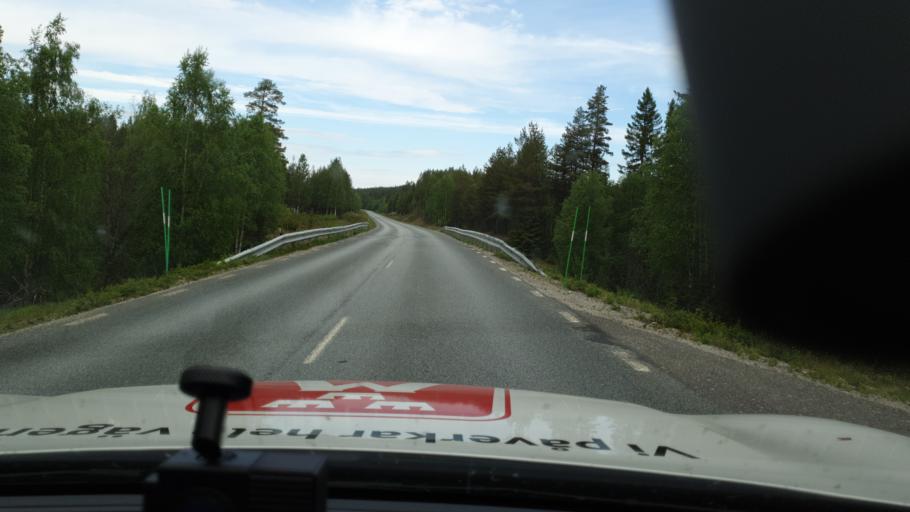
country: SE
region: Vaesterbotten
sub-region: Mala Kommun
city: Mala
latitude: 65.0604
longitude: 18.3791
